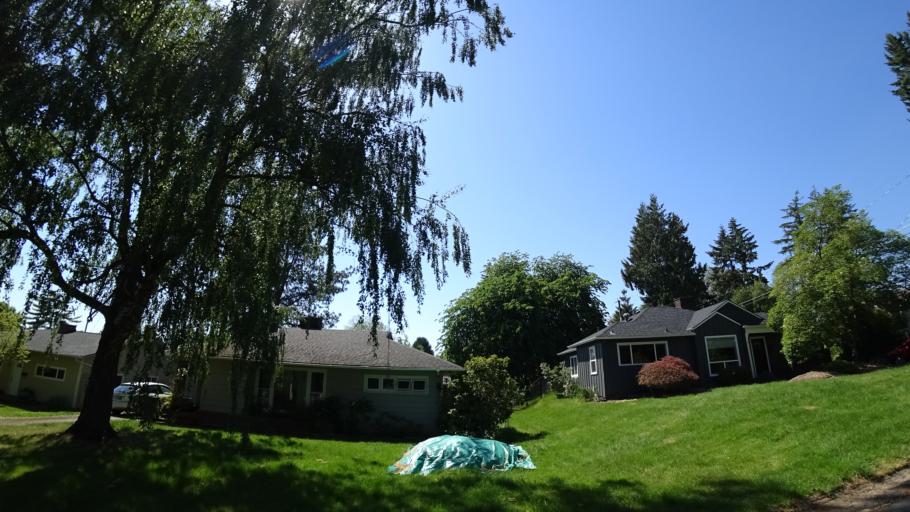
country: US
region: Oregon
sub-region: Washington County
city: Cedar Hills
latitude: 45.4987
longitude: -122.8002
